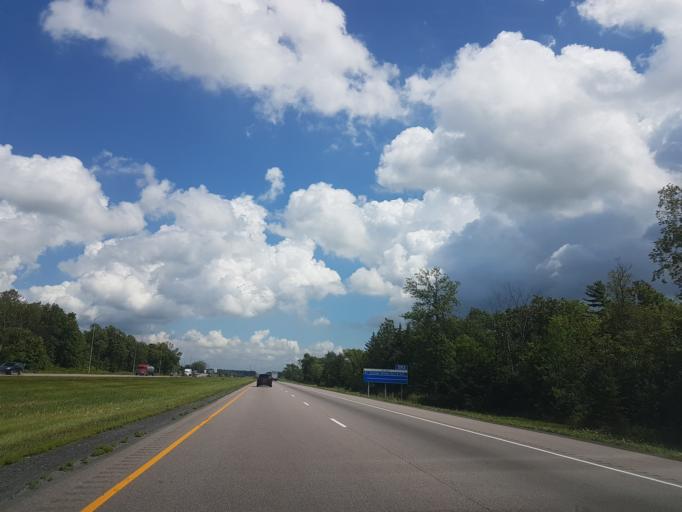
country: CA
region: Ontario
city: Skatepark
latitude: 44.2780
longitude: -76.8136
